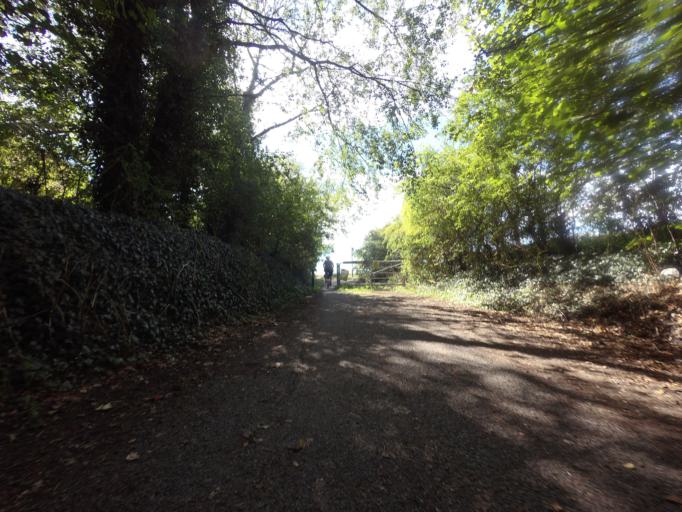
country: GB
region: England
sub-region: Kent
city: Birchington-on-Sea
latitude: 51.3413
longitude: 1.2692
